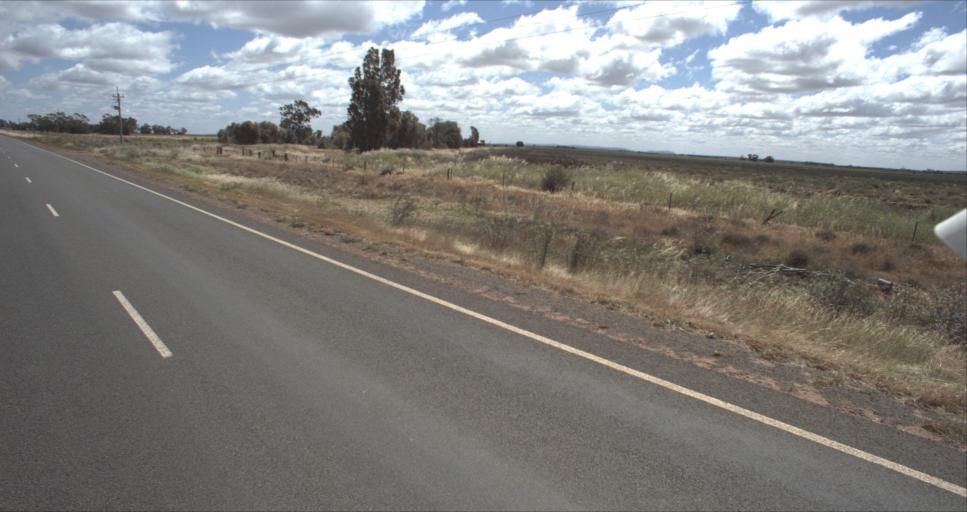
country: AU
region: New South Wales
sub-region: Murrumbidgee Shire
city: Darlington Point
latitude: -34.4880
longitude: 146.1617
